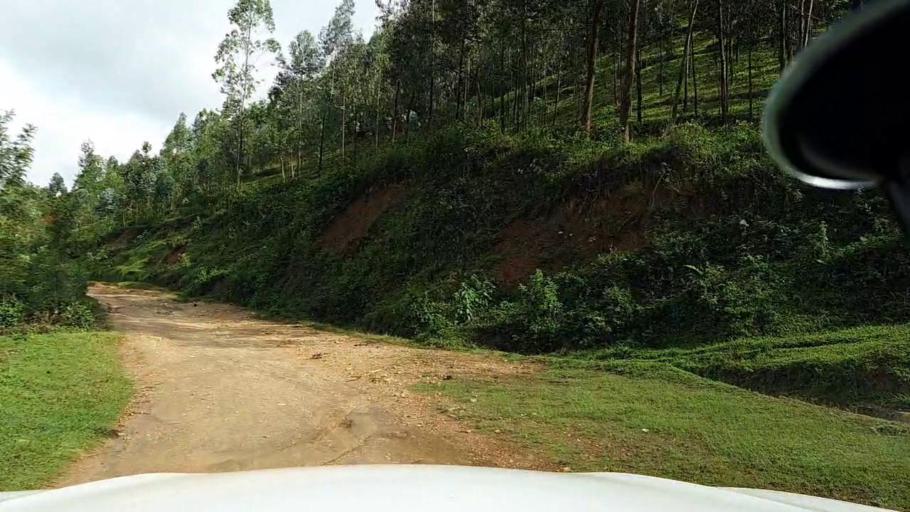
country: RW
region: Western Province
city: Kibuye
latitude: -2.1322
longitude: 29.4997
